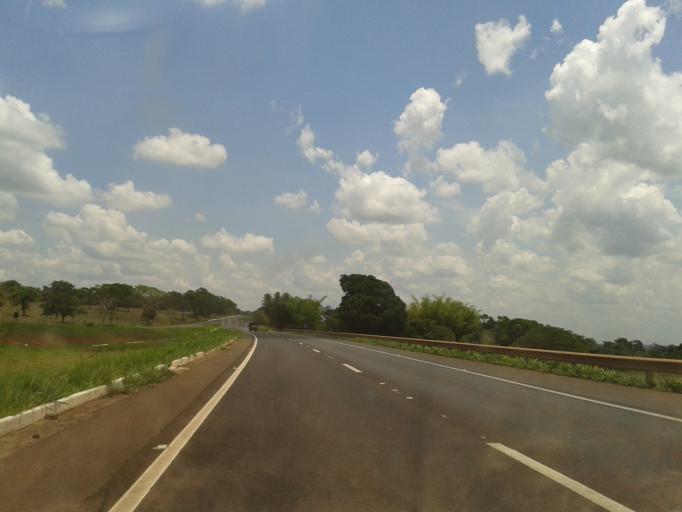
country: BR
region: Minas Gerais
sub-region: Monte Alegre De Minas
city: Monte Alegre de Minas
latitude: -18.8926
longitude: -48.6629
